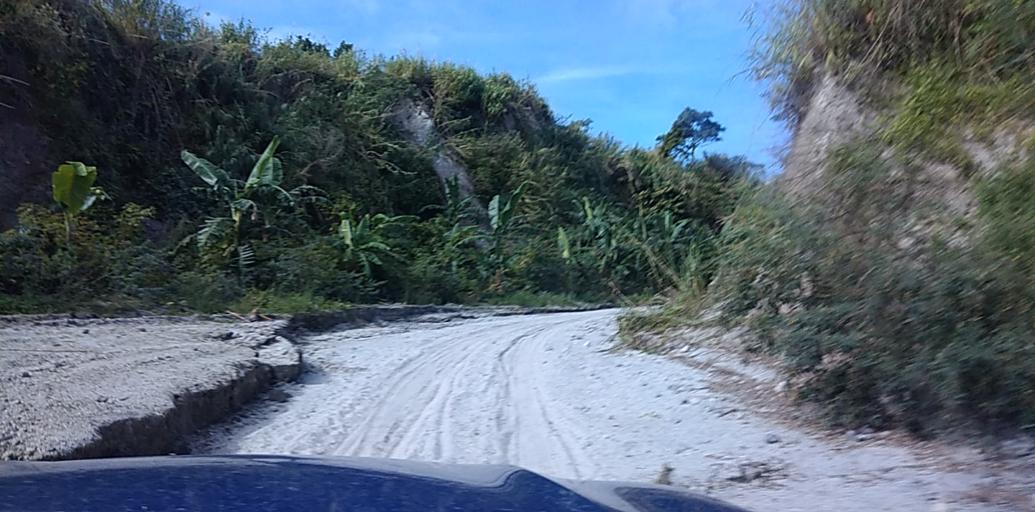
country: PH
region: Central Luzon
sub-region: Province of Pampanga
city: Babo-Pangulo
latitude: 15.1492
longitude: 120.4379
